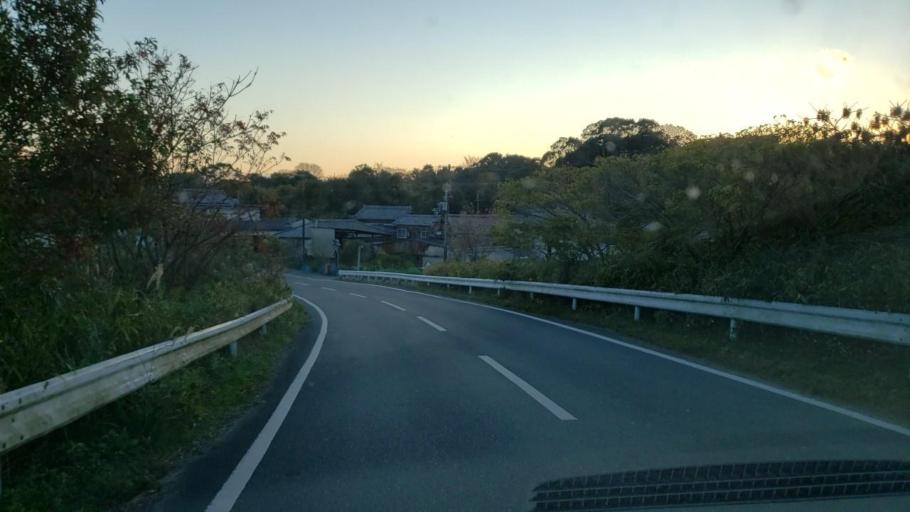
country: JP
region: Hyogo
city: Fukura
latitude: 34.3487
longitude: 134.7828
